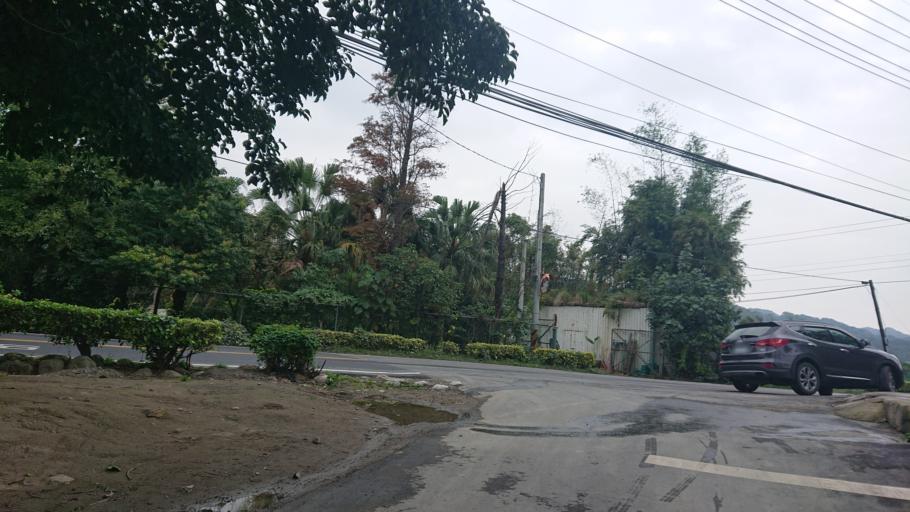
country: TW
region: Taiwan
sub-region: Taoyuan
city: Taoyuan
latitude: 24.9474
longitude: 121.3652
